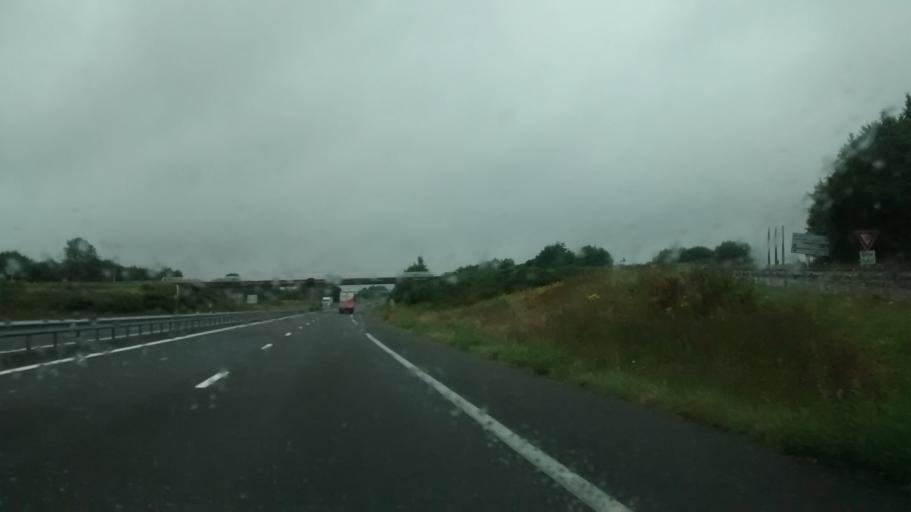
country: FR
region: Brittany
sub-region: Departement d'Ille-et-Vilaine
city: Saint-Etienne-en-Cogles
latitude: 48.4606
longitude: -1.3285
